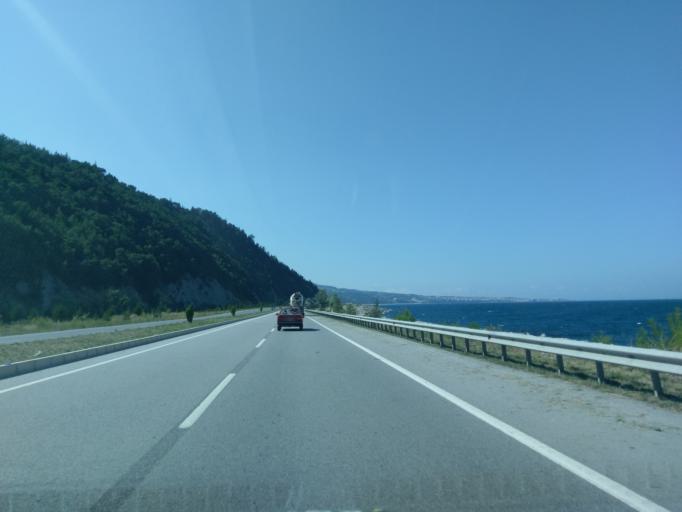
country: TR
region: Sinop
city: Gerze
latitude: 41.7462
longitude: 35.2461
